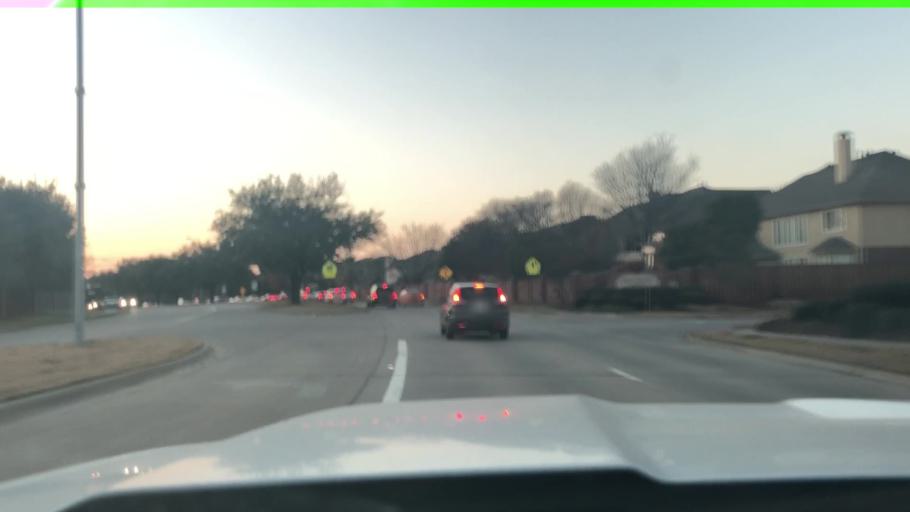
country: US
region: Texas
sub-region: Denton County
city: Flower Mound
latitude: 33.0210
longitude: -97.0773
